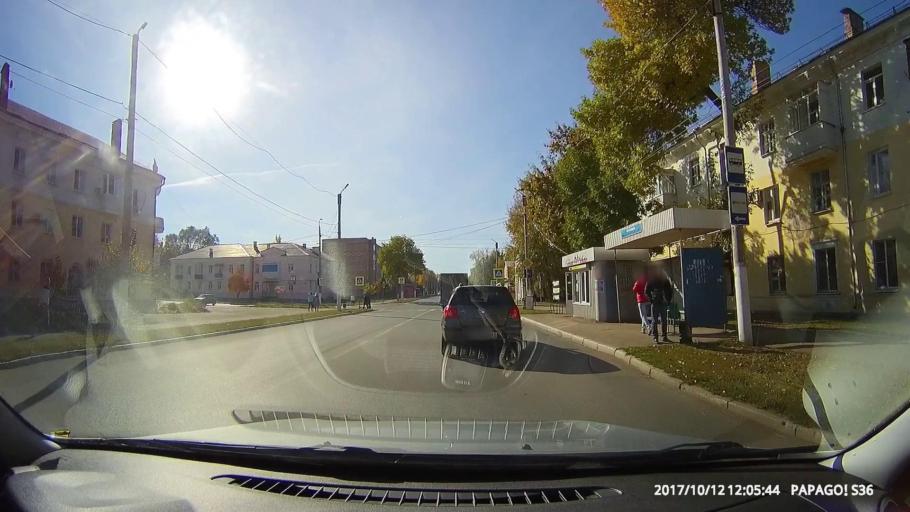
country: RU
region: Samara
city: Chapayevsk
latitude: 52.9757
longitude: 49.7104
